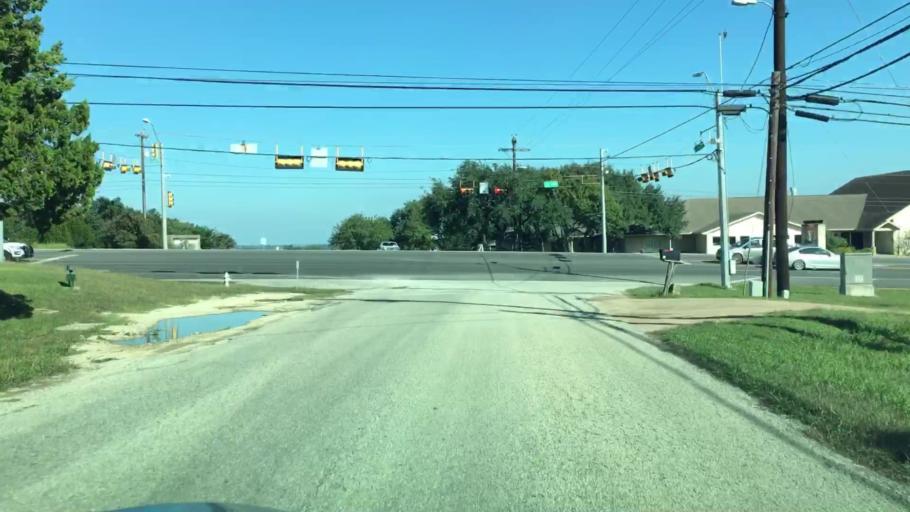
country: US
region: Texas
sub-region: Hays County
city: Dripping Springs
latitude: 30.1968
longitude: -98.0196
